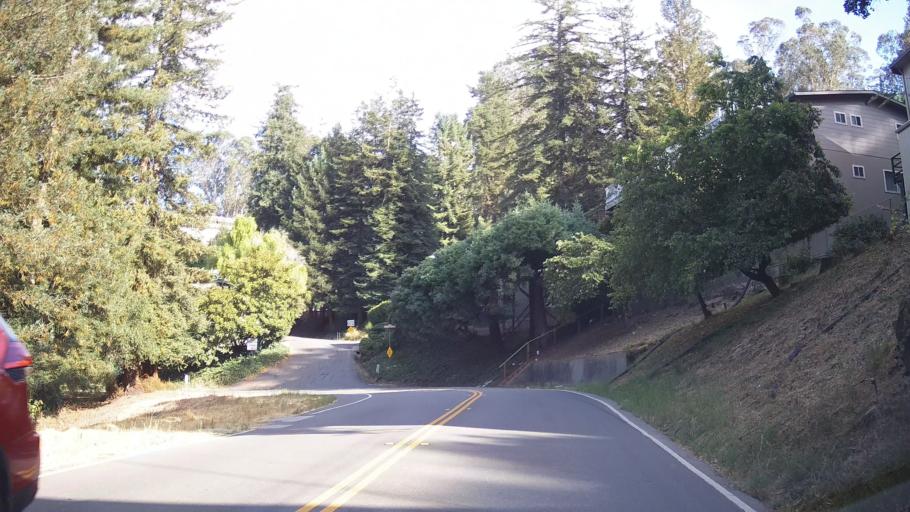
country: US
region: California
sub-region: Contra Costa County
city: Kensington
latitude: 37.8993
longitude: -122.2590
